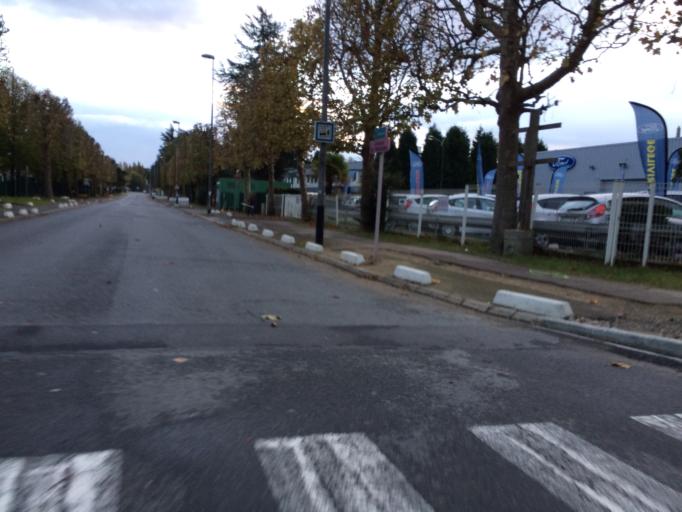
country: FR
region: Ile-de-France
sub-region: Departement de l'Essonne
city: Orsay
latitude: 48.6843
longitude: 2.1997
